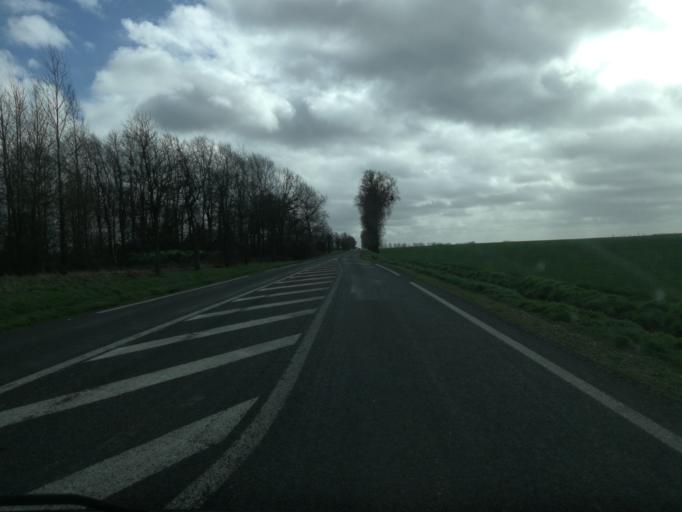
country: FR
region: Haute-Normandie
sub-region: Departement de la Seine-Maritime
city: Fauville-en-Caux
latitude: 49.6424
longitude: 0.6190
